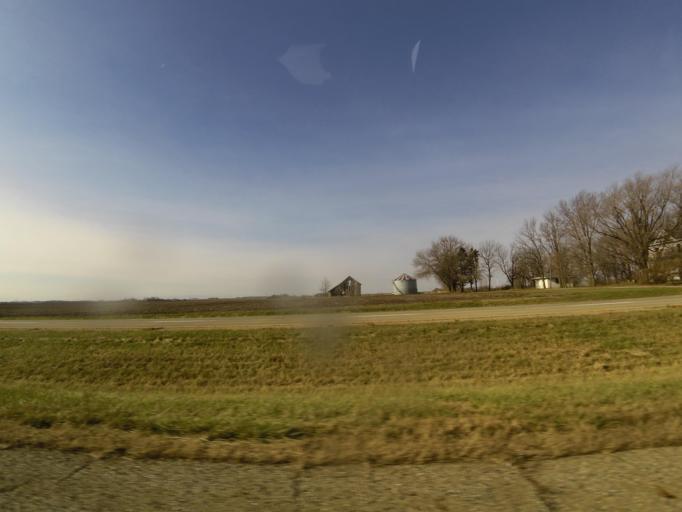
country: US
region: Illinois
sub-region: Macon County
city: Forsyth
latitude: 39.9535
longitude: -88.9555
